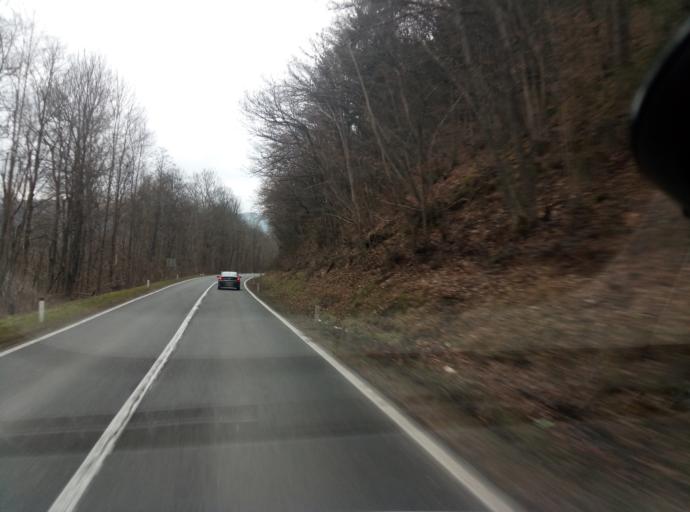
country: SI
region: Smartno pri Litiji
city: Smartno pri Litiji
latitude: 46.0717
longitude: 14.8655
